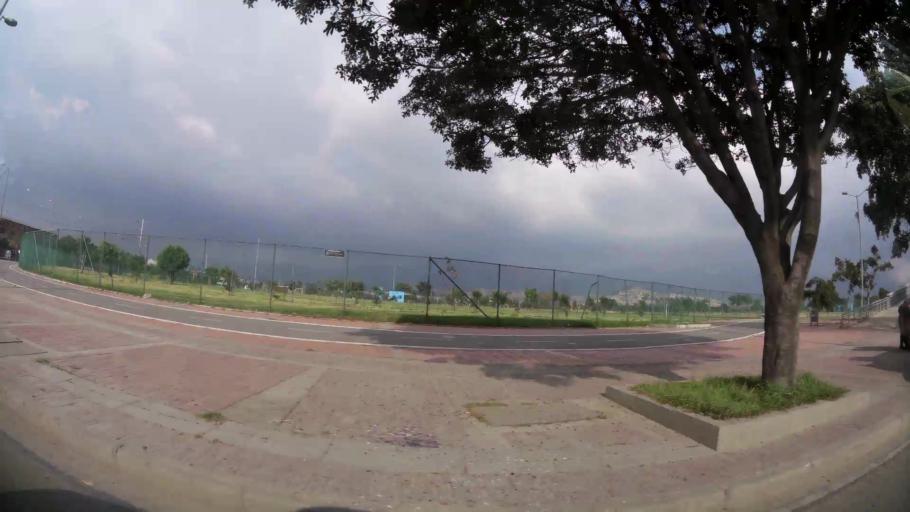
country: CO
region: Bogota D.C.
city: Bogota
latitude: 4.5725
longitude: -74.1391
